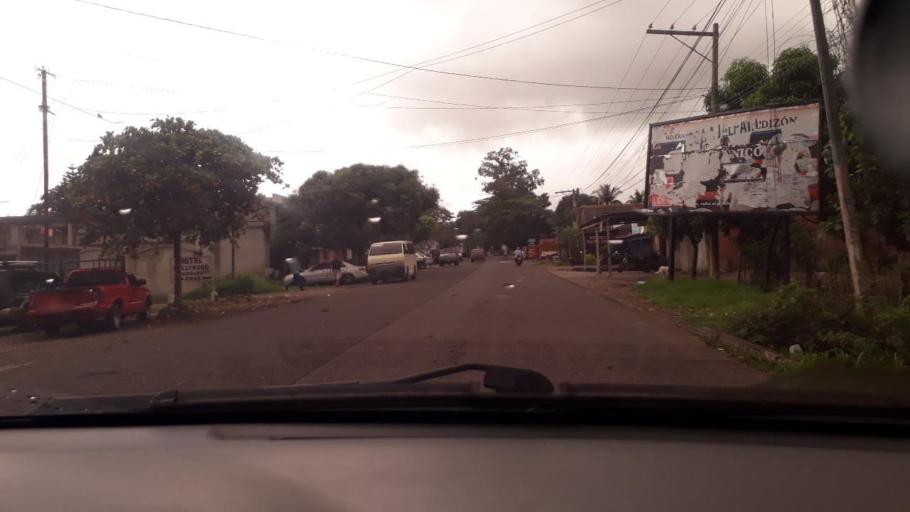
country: GT
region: Jutiapa
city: Jalpatagua
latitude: 14.1332
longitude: -90.0058
